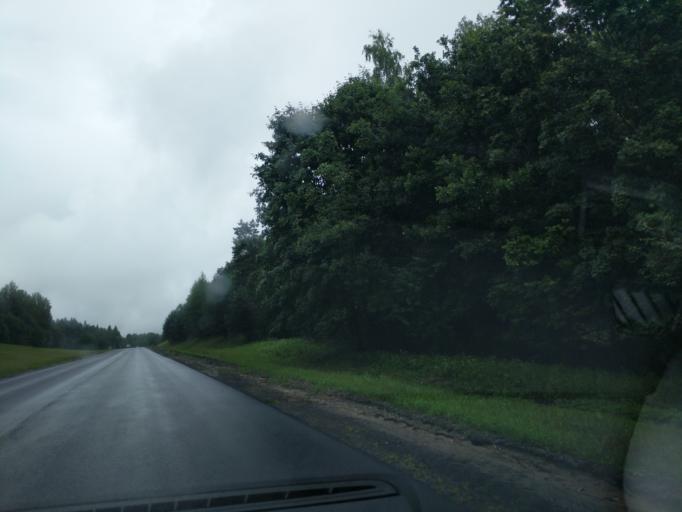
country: BY
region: Minsk
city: Syomkava
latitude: 54.2428
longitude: 27.4853
